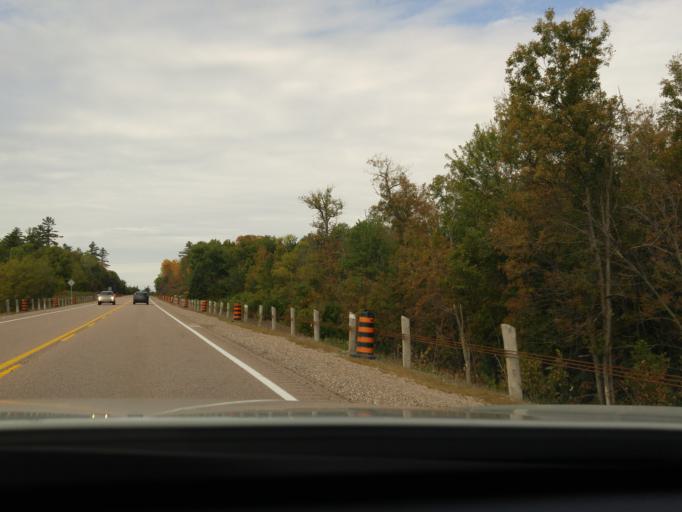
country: CA
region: Ontario
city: Renfrew
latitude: 45.5391
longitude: -76.7115
